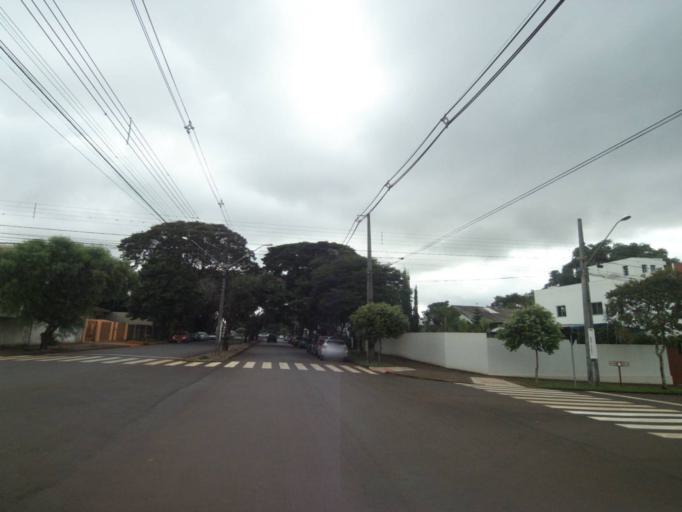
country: BR
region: Parana
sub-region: Campo Mourao
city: Campo Mourao
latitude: -24.0468
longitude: -52.3738
